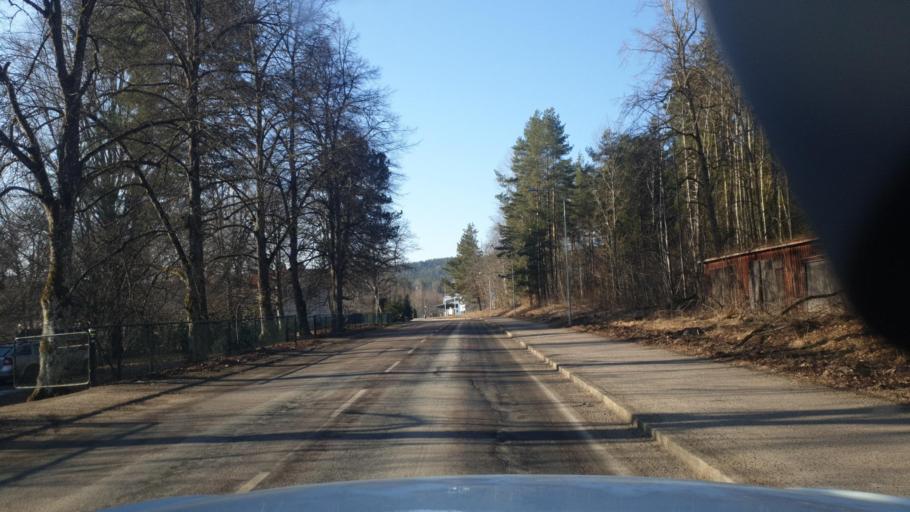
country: SE
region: Vaermland
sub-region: Eda Kommun
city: Amotfors
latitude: 59.7591
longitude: 12.3581
